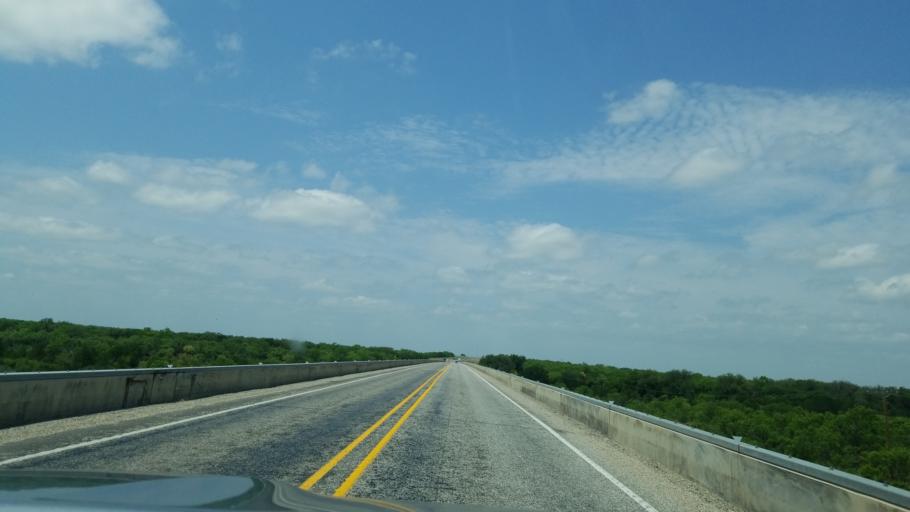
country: US
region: Texas
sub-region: Zavala County
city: La Pryor
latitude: 28.9341
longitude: -99.7937
